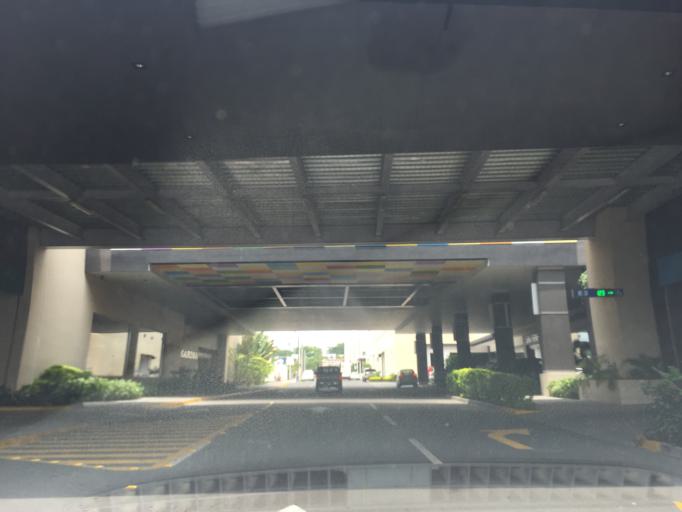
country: MX
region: Colima
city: Colima
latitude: 19.2519
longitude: -103.7216
